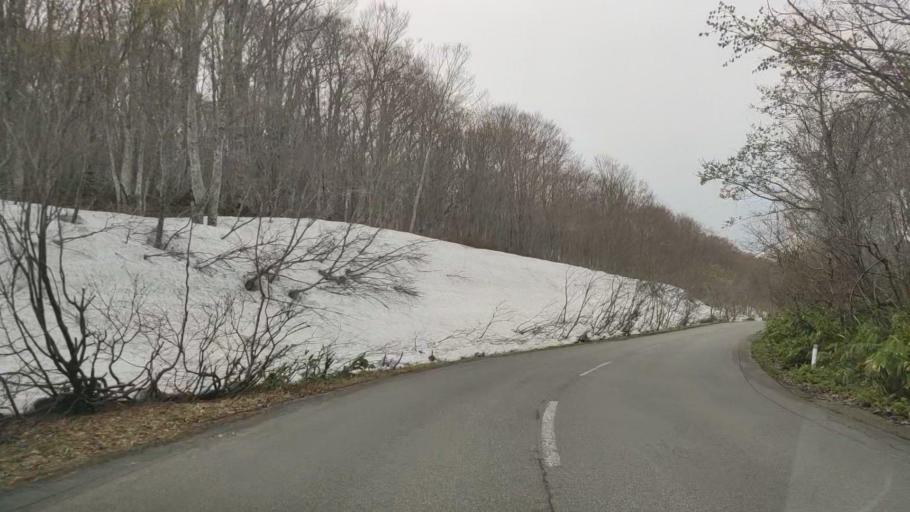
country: JP
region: Aomori
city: Aomori Shi
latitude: 40.6539
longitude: 140.9548
